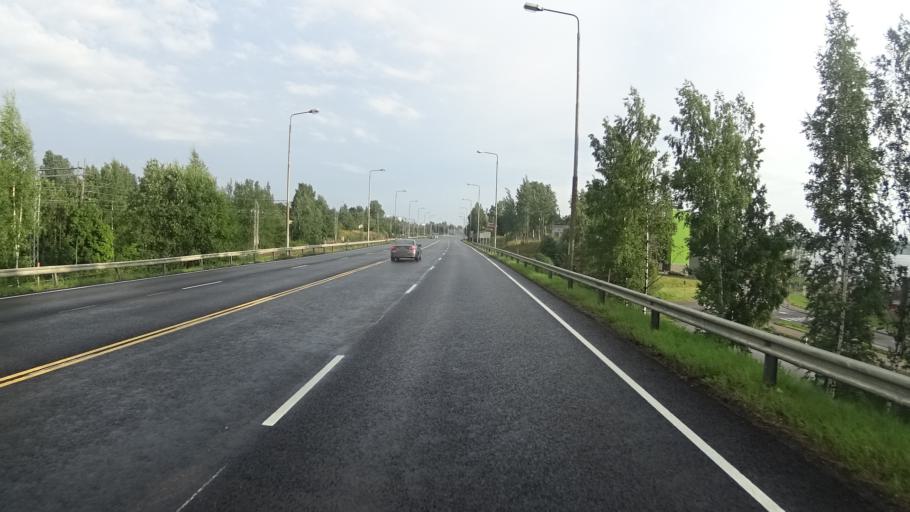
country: FI
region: Kymenlaakso
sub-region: Kotka-Hamina
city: Kotka
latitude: 60.4710
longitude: 26.9183
